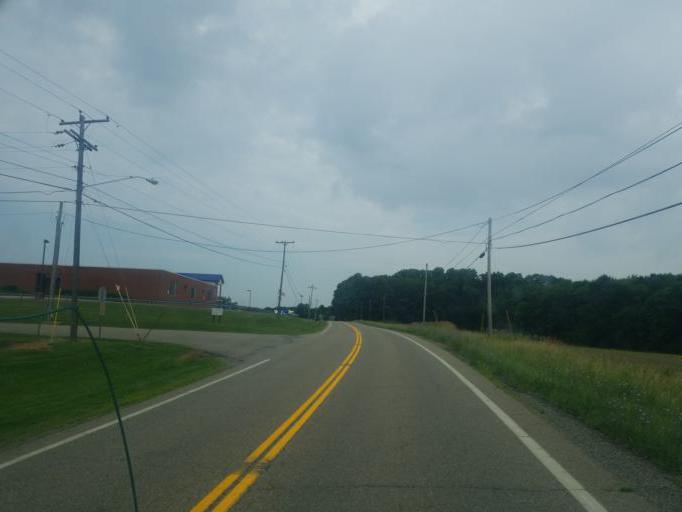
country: US
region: Ohio
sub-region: Columbiana County
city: Salem
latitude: 40.7822
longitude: -80.9279
